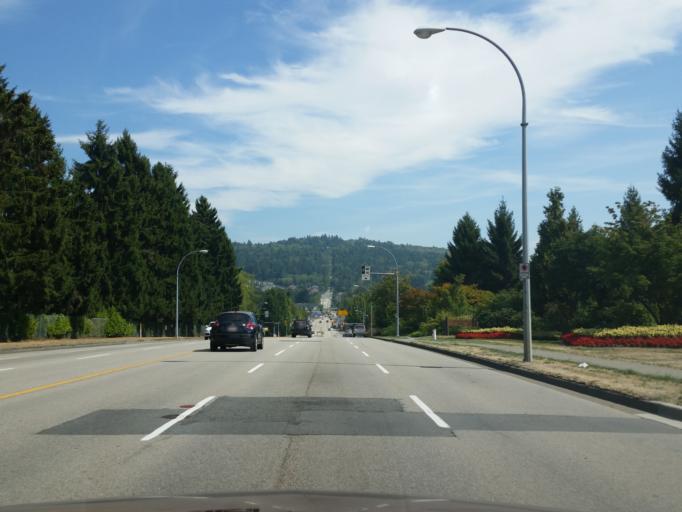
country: CA
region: British Columbia
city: Burnaby
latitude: 49.2803
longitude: -122.9734
